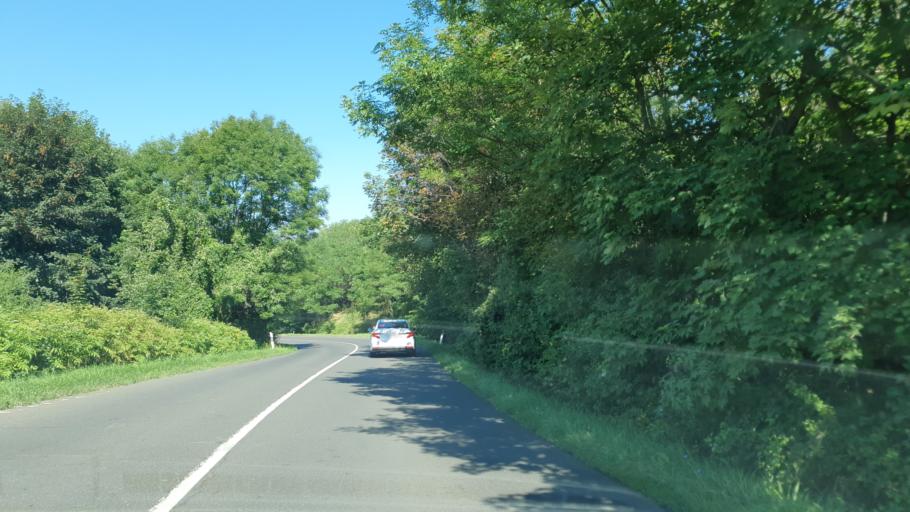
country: HU
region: Nograd
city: Szecseny
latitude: 48.0700
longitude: 19.5570
